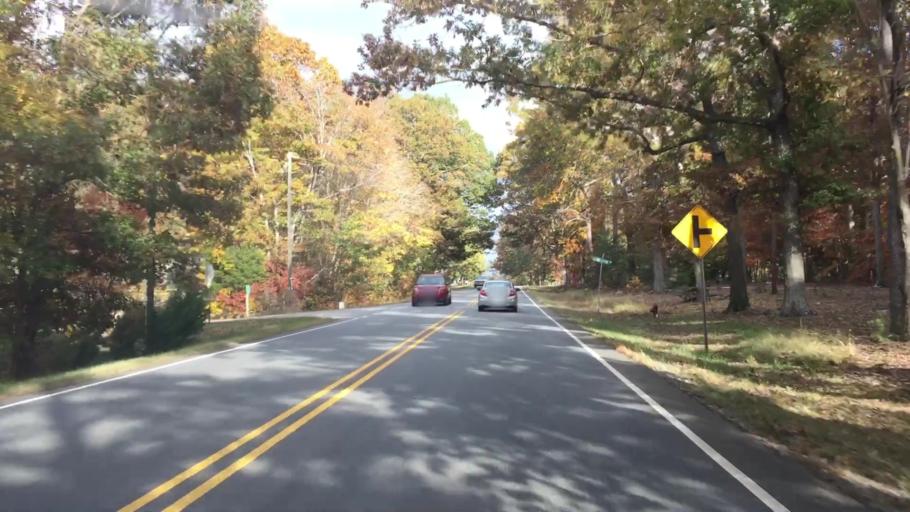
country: US
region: North Carolina
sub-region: Guilford County
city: Summerfield
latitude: 36.2669
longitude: -79.8500
